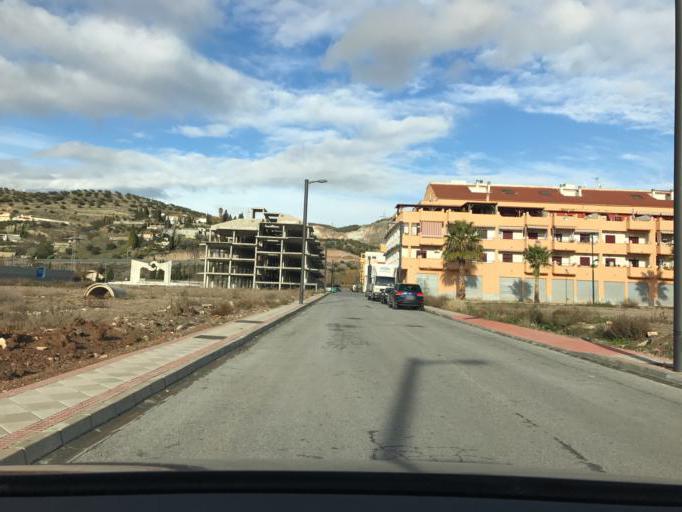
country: ES
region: Andalusia
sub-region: Provincia de Granada
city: Atarfe
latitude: 37.2230
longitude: -3.7004
